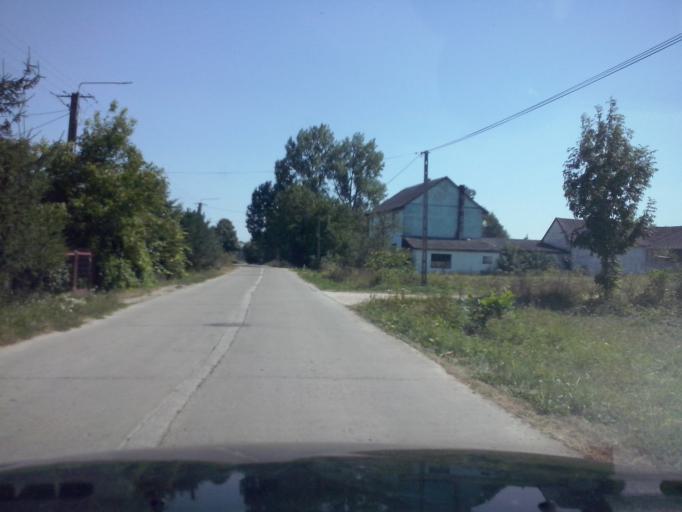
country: PL
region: Swietokrzyskie
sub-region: Powiat buski
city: Gnojno
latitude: 50.5991
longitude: 20.8056
